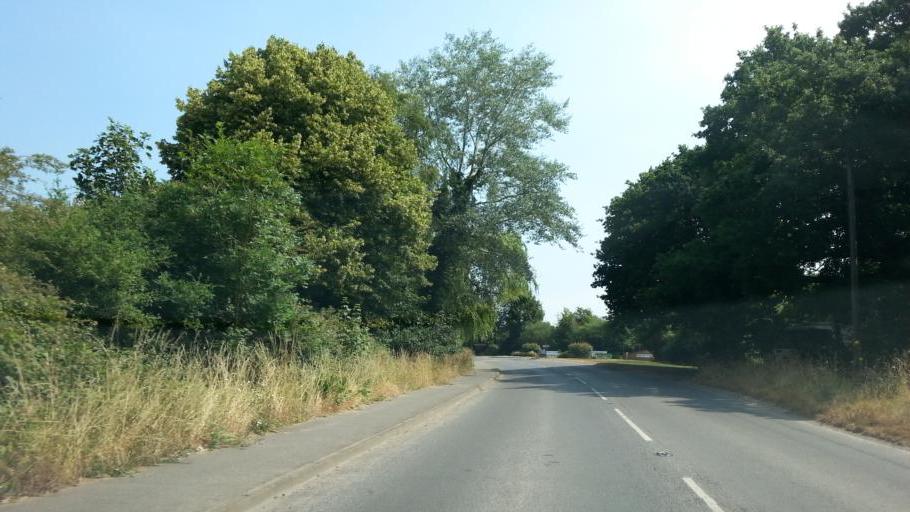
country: GB
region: England
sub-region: Cambridgeshire
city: Brampton
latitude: 52.3123
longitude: -0.2265
